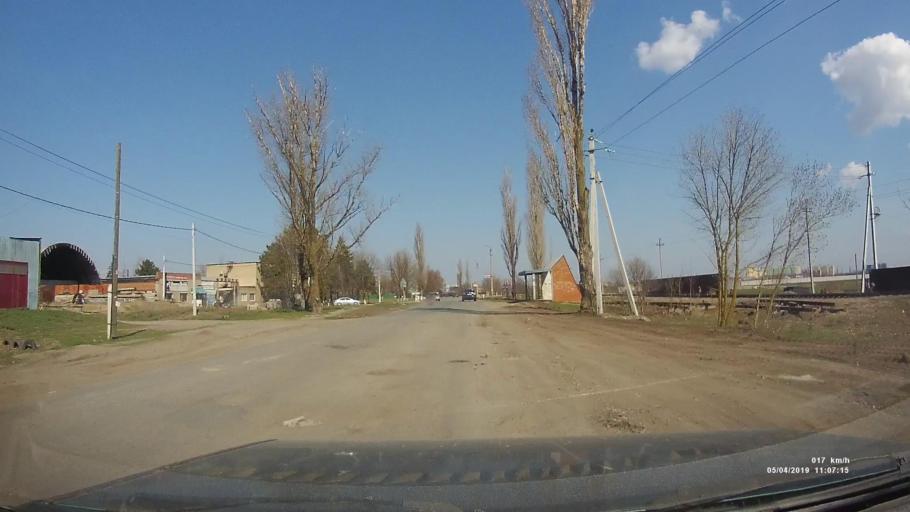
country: RU
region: Rostov
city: Azov
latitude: 47.0806
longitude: 39.4374
